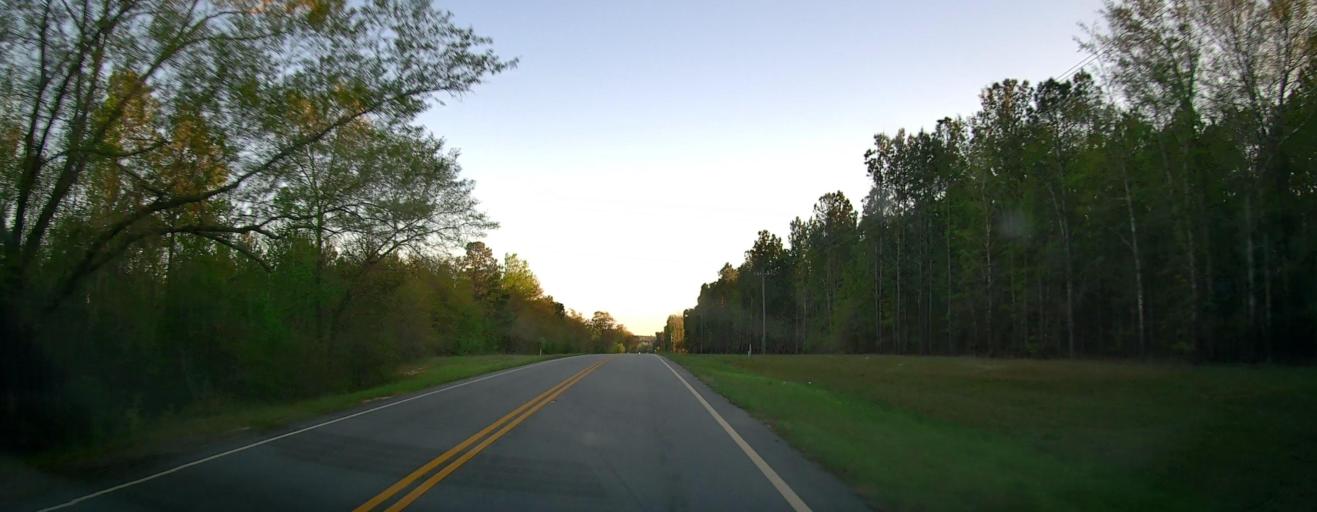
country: US
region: Georgia
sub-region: Talbot County
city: Talbotton
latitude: 32.5466
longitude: -84.5698
